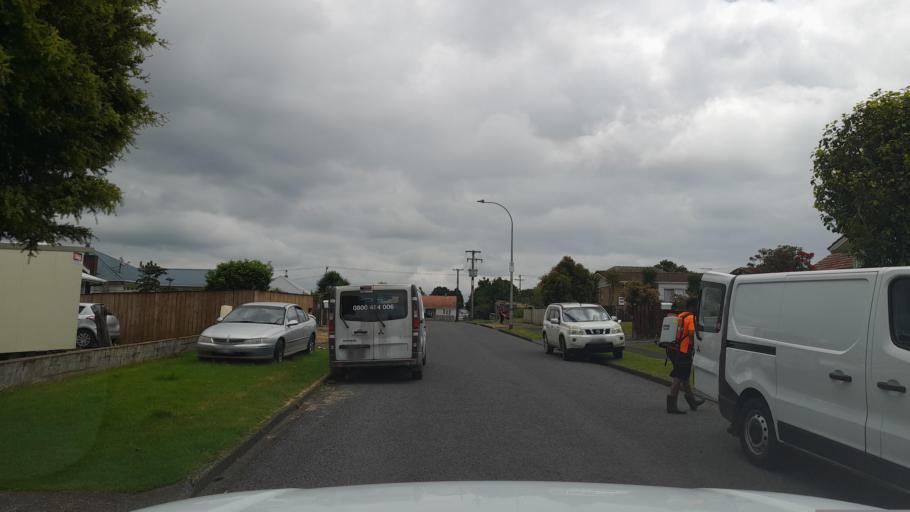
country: NZ
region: Northland
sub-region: Far North District
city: Waimate North
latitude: -35.4068
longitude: 173.8069
